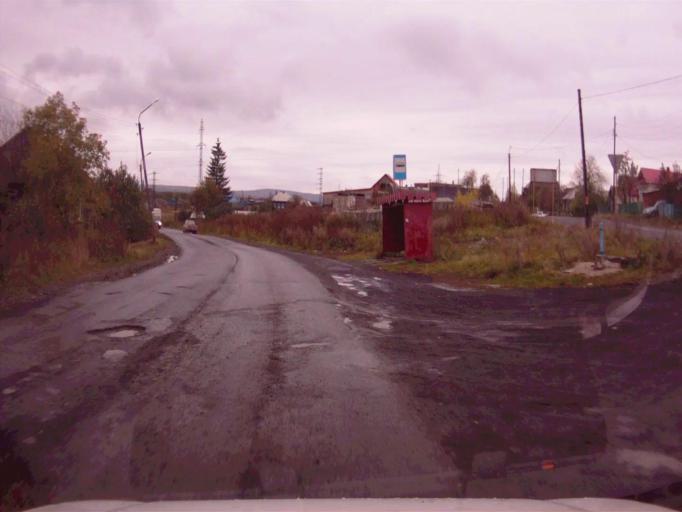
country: RU
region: Chelyabinsk
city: Verkhniy Ufaley
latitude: 56.0596
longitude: 60.2018
